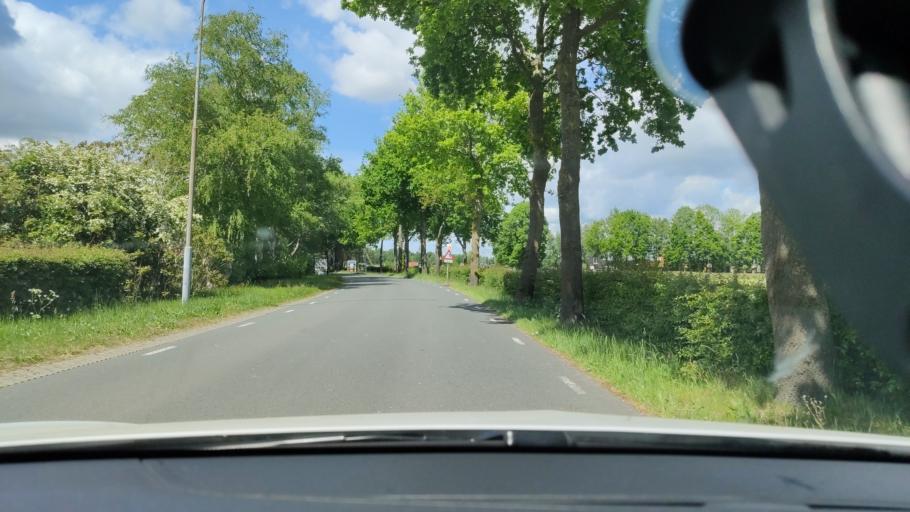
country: NL
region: Drenthe
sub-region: Gemeente Tynaarlo
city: Zuidlaren
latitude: 53.1066
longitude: 6.6836
